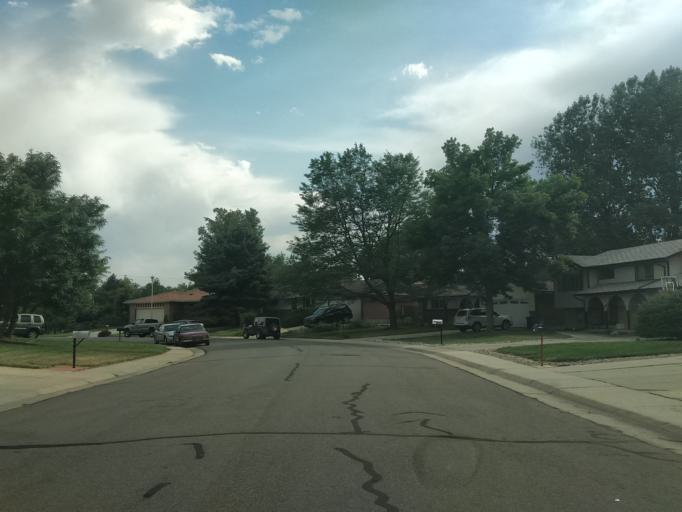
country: US
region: Colorado
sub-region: Jefferson County
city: Lakewood
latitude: 39.6983
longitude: -105.1097
